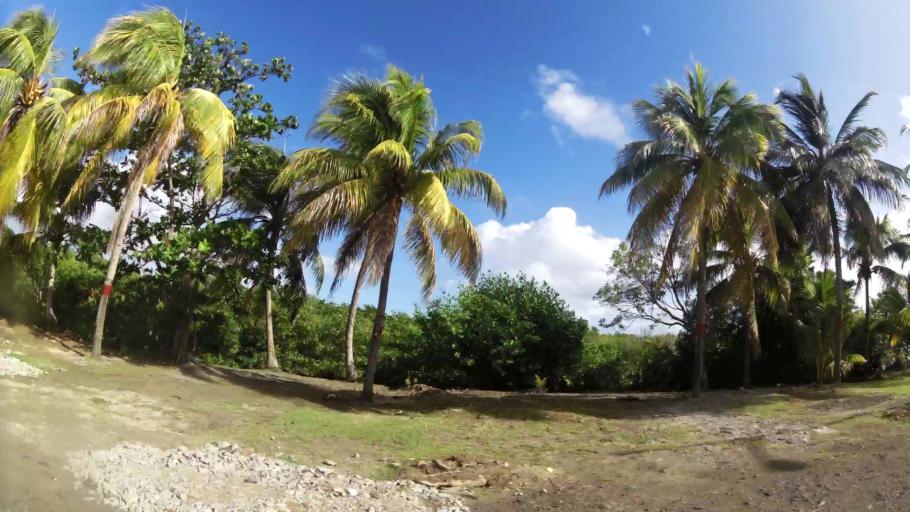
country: MQ
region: Martinique
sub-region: Martinique
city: Le Francois
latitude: 14.6169
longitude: -60.9039
